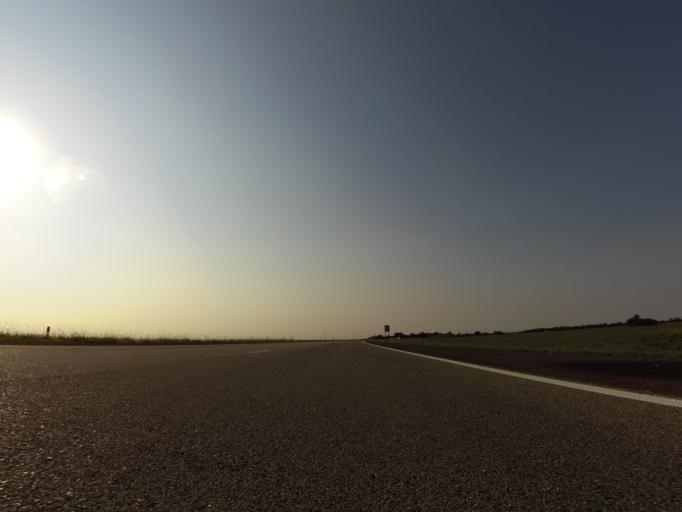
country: US
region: Kansas
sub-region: Reno County
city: South Hutchinson
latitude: 37.9711
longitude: -97.9358
